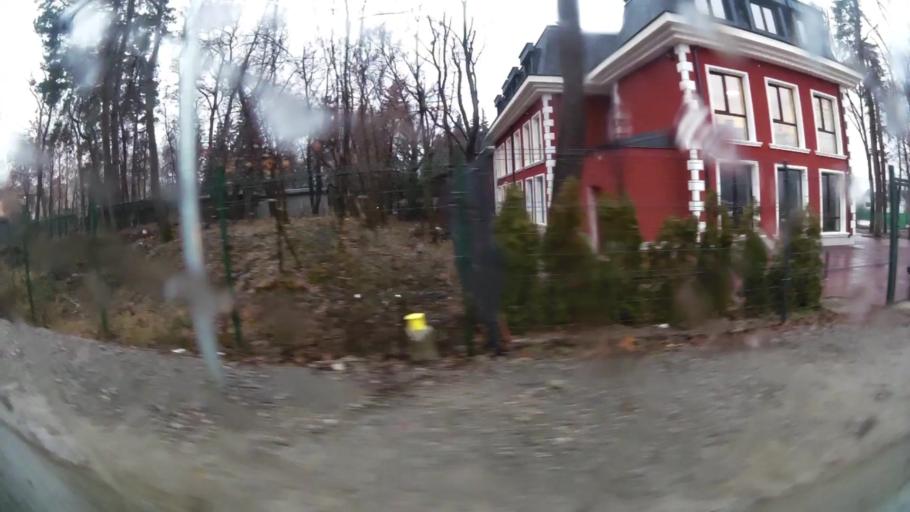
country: BG
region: Sofia-Capital
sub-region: Stolichna Obshtina
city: Sofia
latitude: 42.6502
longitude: 23.3196
